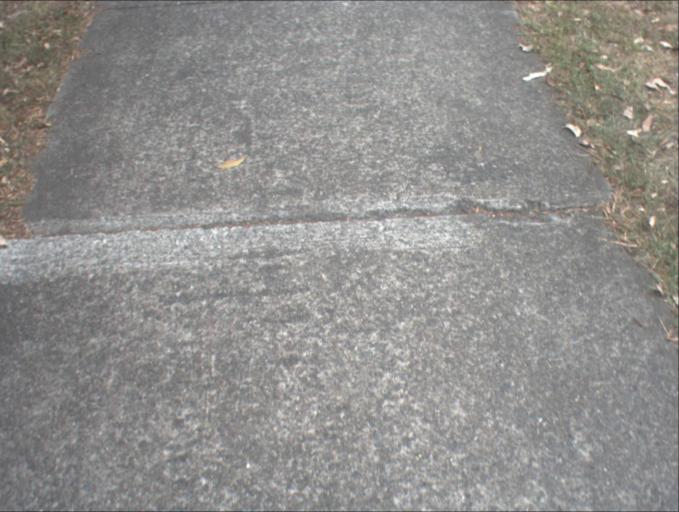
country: AU
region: Queensland
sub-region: Logan
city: Beenleigh
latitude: -27.7101
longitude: 153.1948
